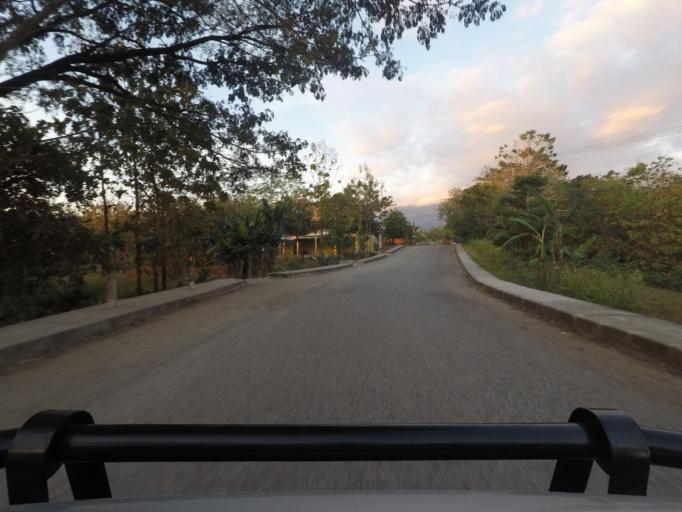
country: TL
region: Bobonaro
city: Maliana
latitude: -8.9918
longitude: 125.1945
